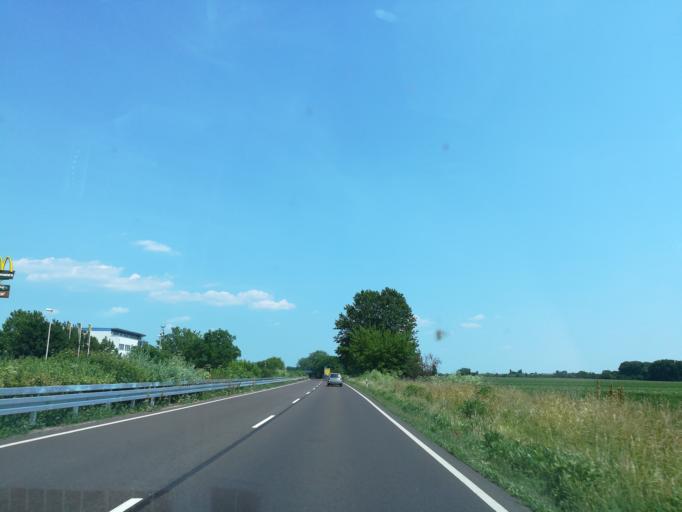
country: DE
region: Saxony-Anhalt
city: Diesdorf
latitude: 52.0784
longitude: 11.5814
